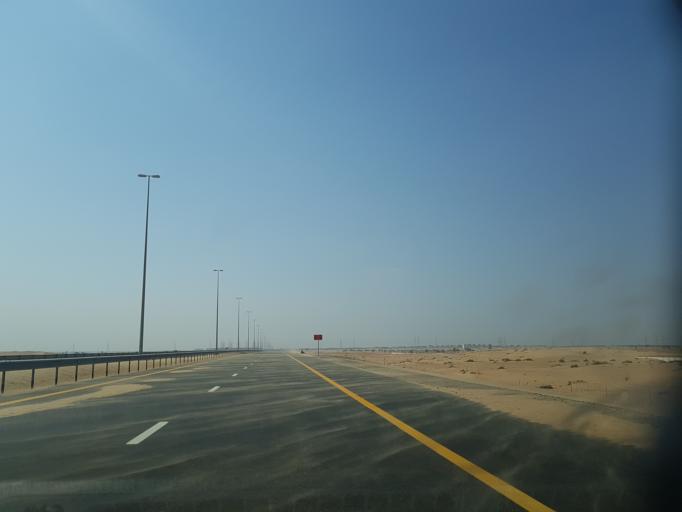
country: AE
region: Ash Shariqah
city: Sharjah
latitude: 25.2783
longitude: 55.6118
